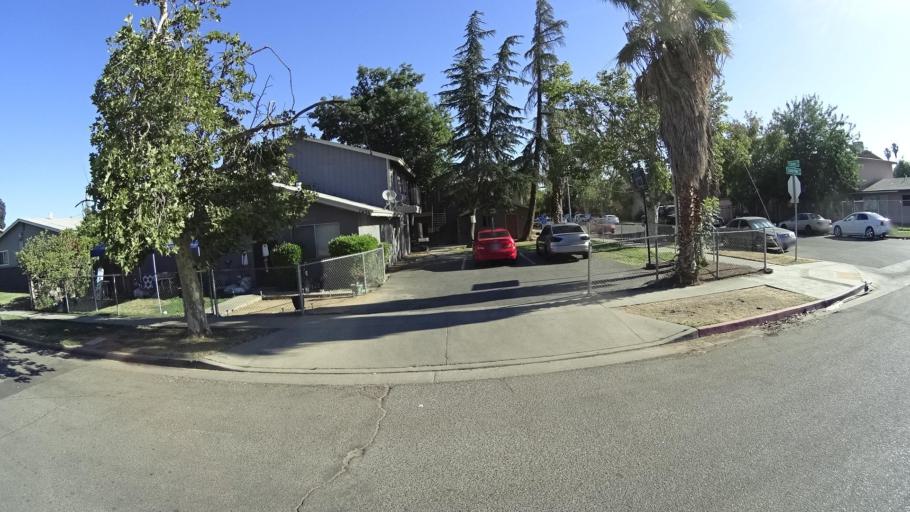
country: US
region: California
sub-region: Fresno County
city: Fresno
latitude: 36.7695
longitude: -119.7936
